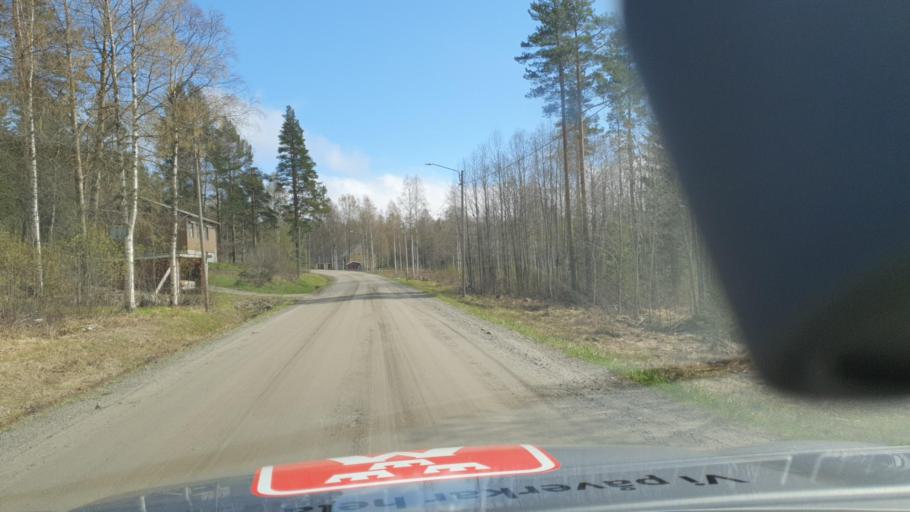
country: SE
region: Vaesterbotten
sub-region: Bjurholms Kommun
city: Bjurholm
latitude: 63.6865
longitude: 18.9623
